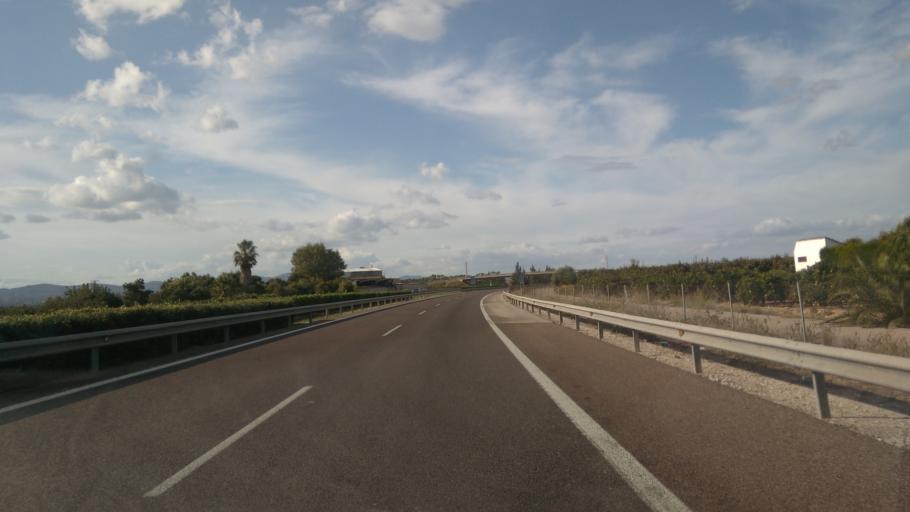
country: ES
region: Valencia
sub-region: Provincia de Valencia
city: Guadassuar
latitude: 39.1801
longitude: -0.4849
